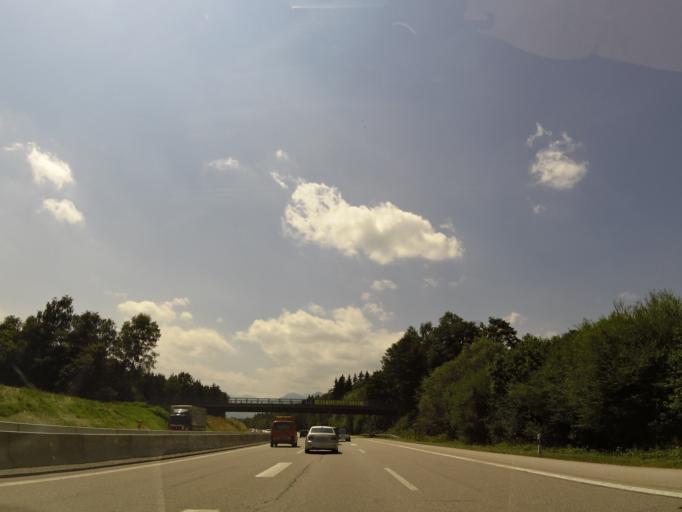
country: DE
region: Bavaria
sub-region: Upper Bavaria
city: Raubling
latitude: 47.8010
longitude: 12.0903
